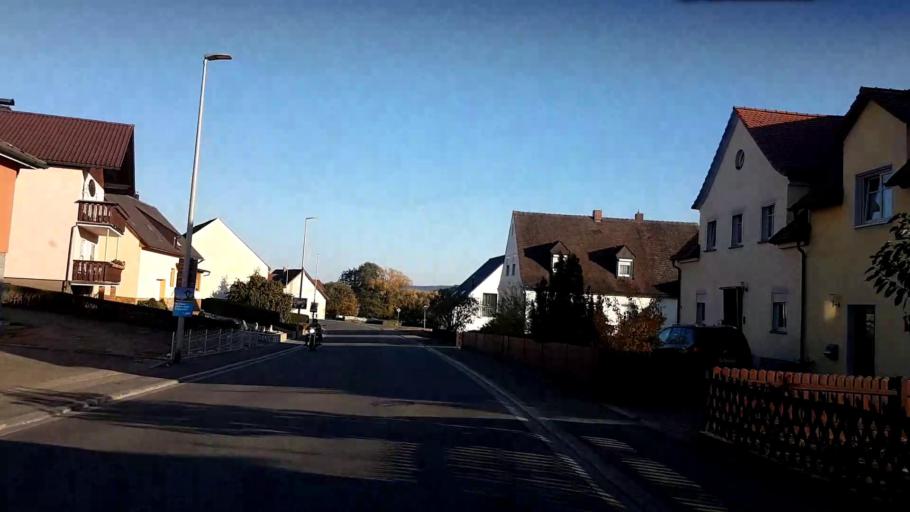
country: DE
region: Bavaria
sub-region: Upper Franconia
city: Stegaurach
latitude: 49.8699
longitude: 10.8159
